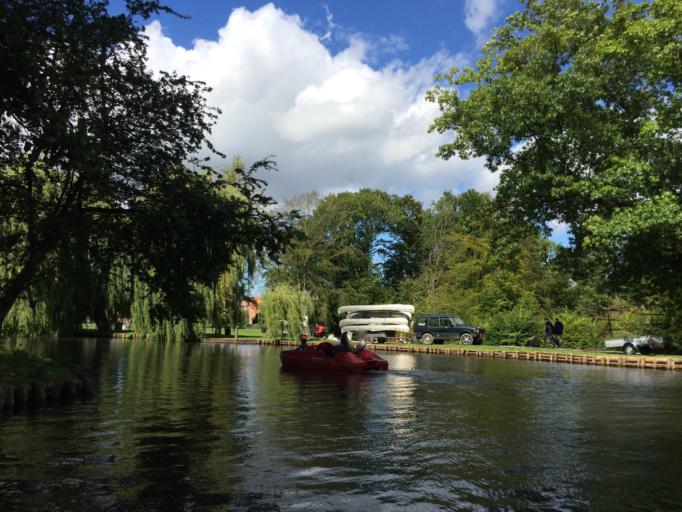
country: DK
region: South Denmark
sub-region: Odense Kommune
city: Odense
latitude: 55.3907
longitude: 10.3819
